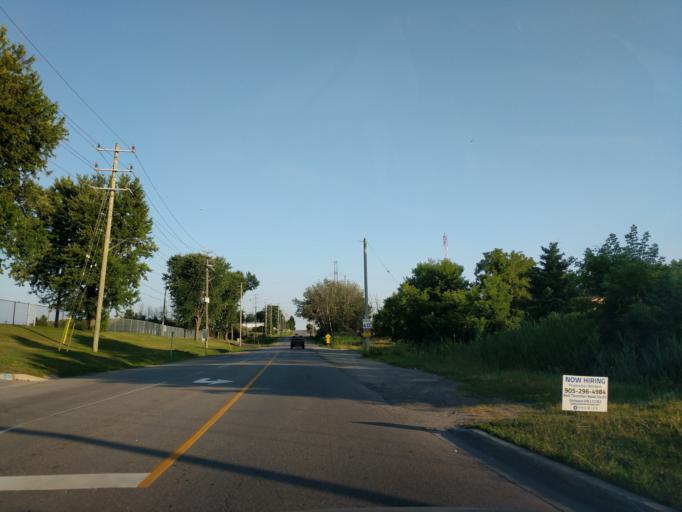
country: CA
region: Ontario
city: Oshawa
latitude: 43.8837
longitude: -78.8898
